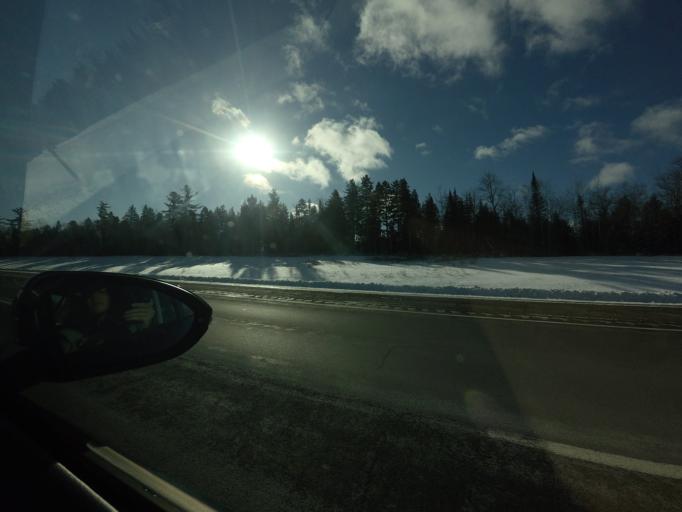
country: CA
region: New Brunswick
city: Fredericton
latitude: 45.8762
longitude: -66.6304
